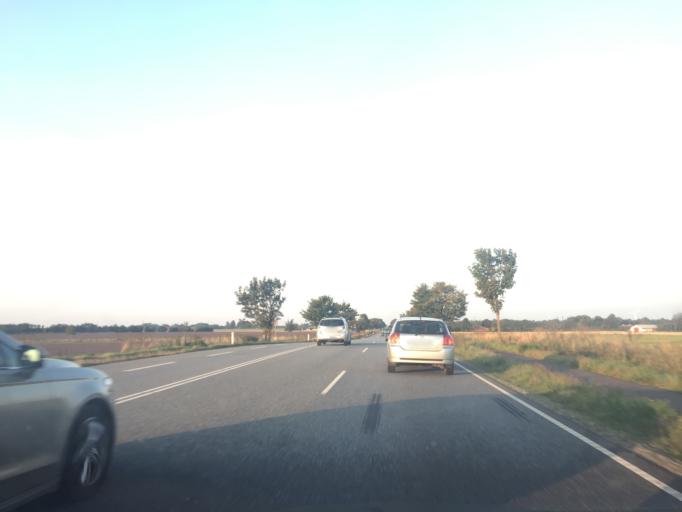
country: DK
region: Zealand
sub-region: Roskilde Kommune
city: Svogerslev
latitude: 55.6083
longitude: 12.0349
